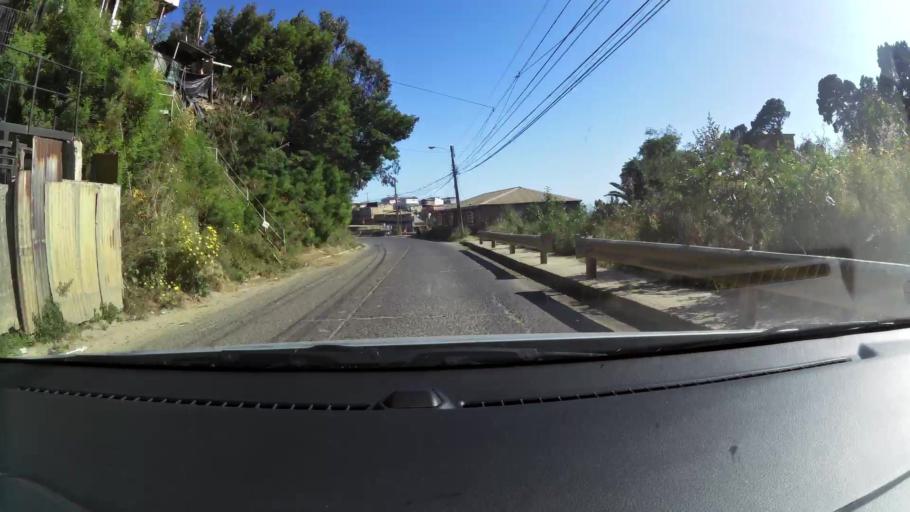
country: CL
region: Valparaiso
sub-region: Provincia de Valparaiso
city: Valparaiso
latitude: -33.0465
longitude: -71.6352
